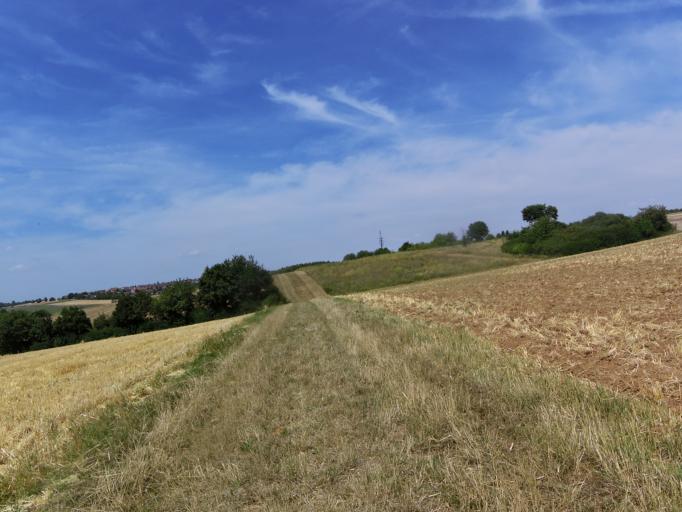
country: DE
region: Bavaria
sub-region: Regierungsbezirk Unterfranken
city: Estenfeld
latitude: 49.8145
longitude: 10.0038
